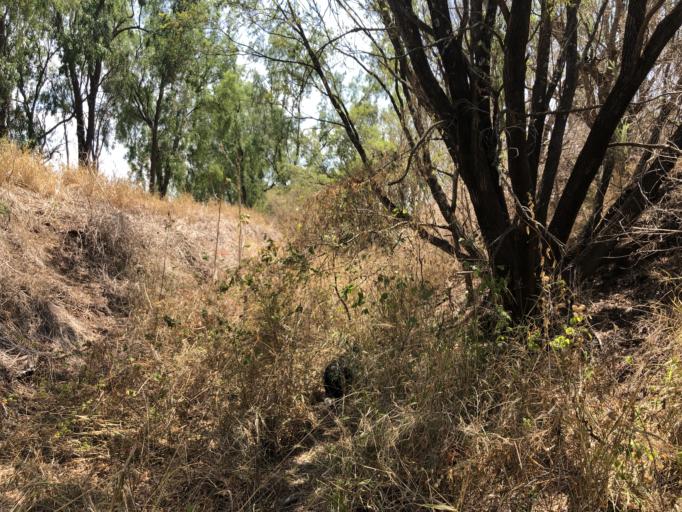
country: AU
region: Queensland
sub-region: Lockyer Valley
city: Gatton
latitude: -27.5859
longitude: 152.3471
